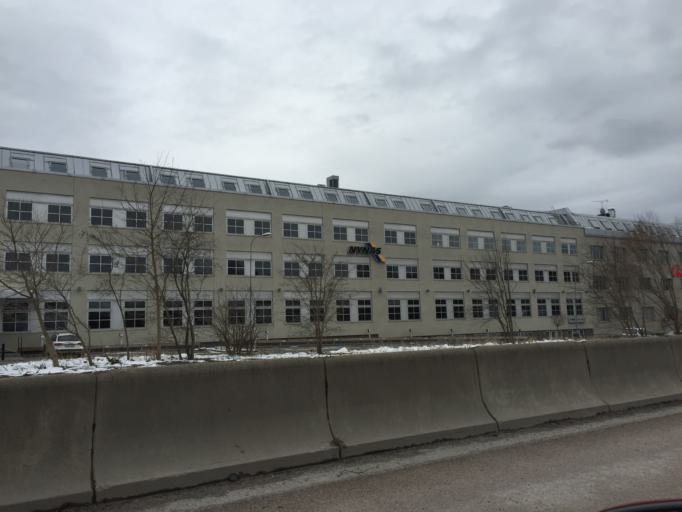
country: SE
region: Stockholm
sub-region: Stockholms Kommun
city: Arsta
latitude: 59.2955
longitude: 18.0683
